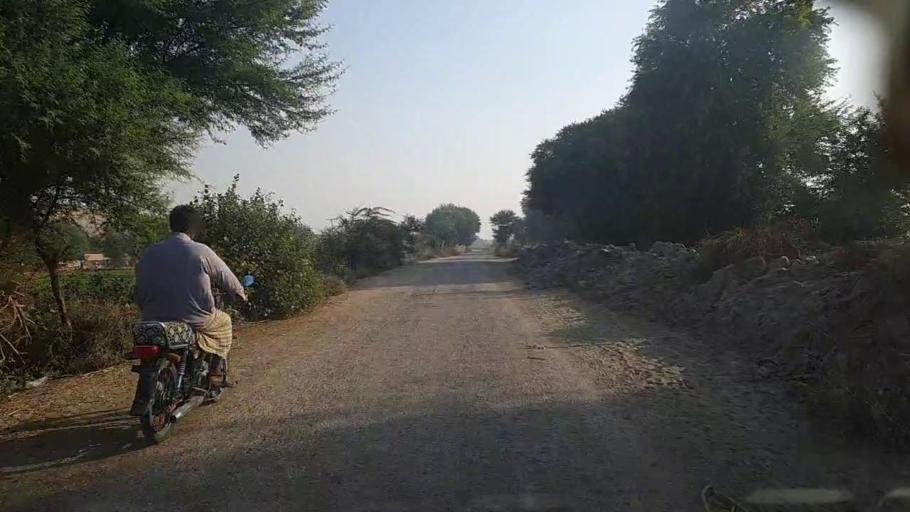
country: PK
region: Sindh
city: Karaundi
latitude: 26.7653
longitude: 68.4746
